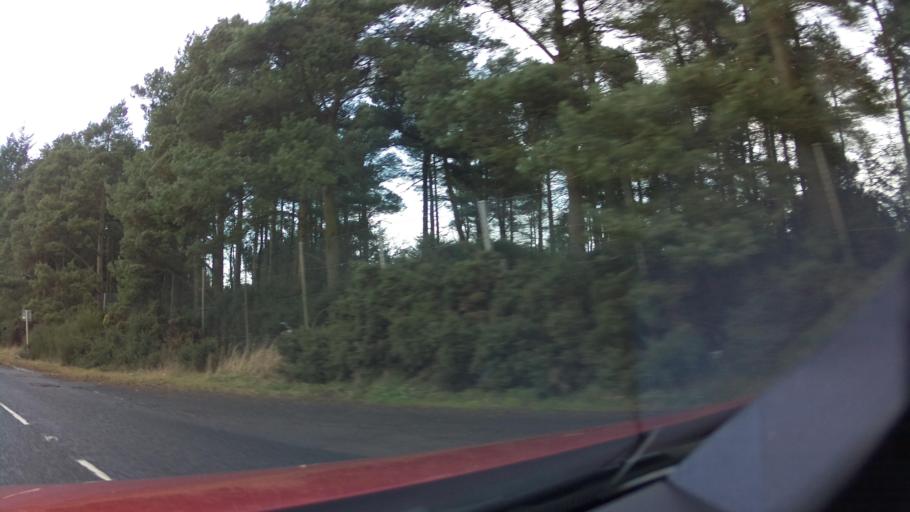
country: GB
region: Scotland
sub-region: Angus
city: Letham
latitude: 56.5547
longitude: -2.7623
